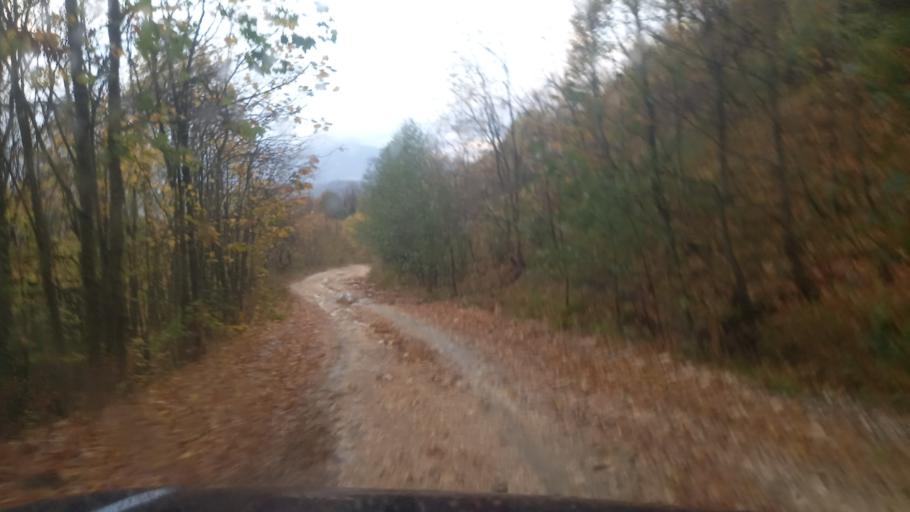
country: RU
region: Krasnodarskiy
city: Neftegorsk
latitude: 44.0221
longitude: 39.8391
